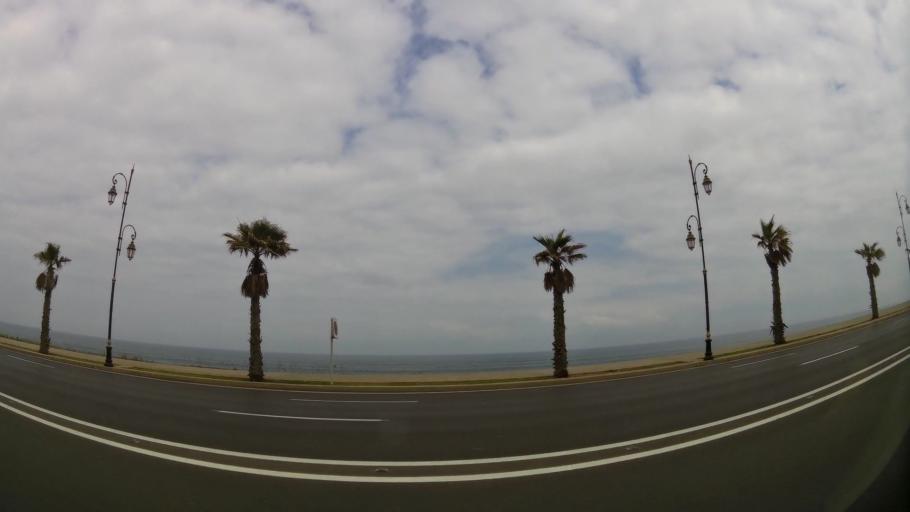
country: MA
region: Rabat-Sale-Zemmour-Zaer
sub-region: Rabat
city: Rabat
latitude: 33.9991
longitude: -6.8763
